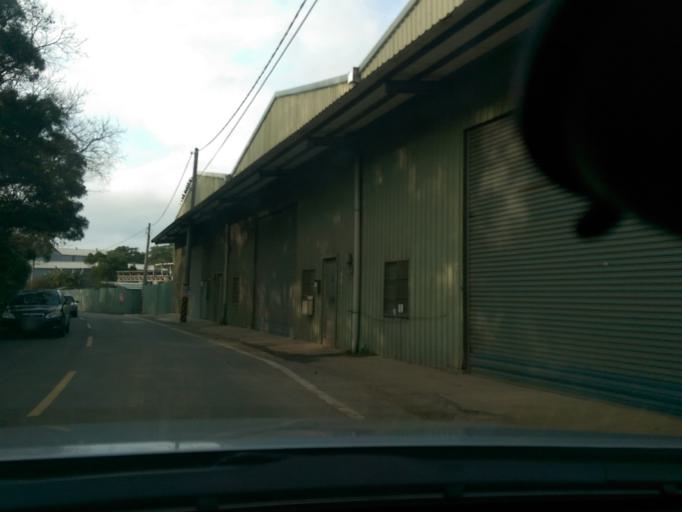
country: TW
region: Taiwan
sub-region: Taoyuan
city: Taoyuan
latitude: 25.0877
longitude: 121.3725
